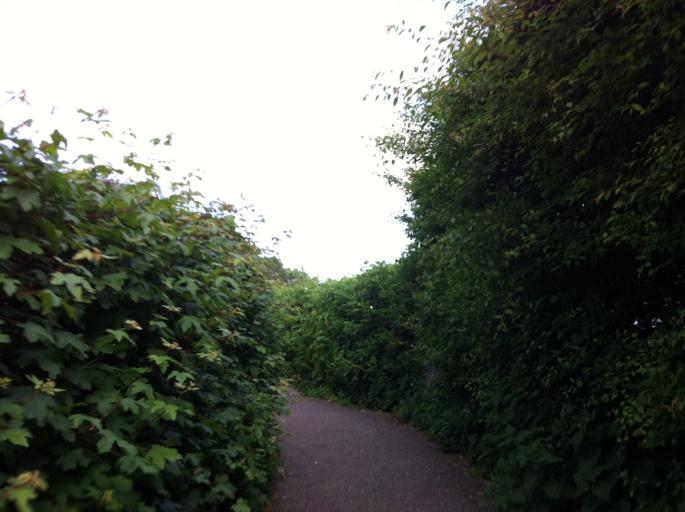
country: DK
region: Capital Region
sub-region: Gribskov Kommune
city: Gilleleje
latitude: 56.1273
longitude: 12.2929
